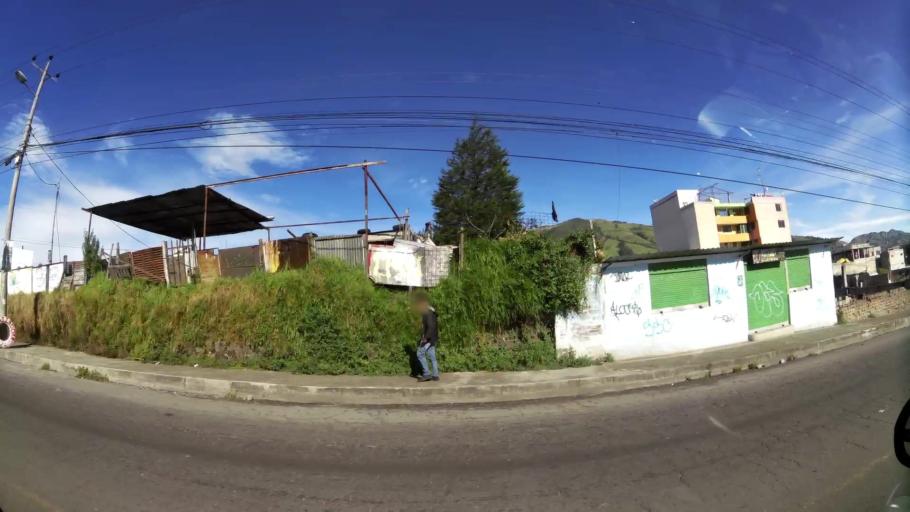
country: EC
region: Pichincha
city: Quito
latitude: -0.3222
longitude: -78.5567
